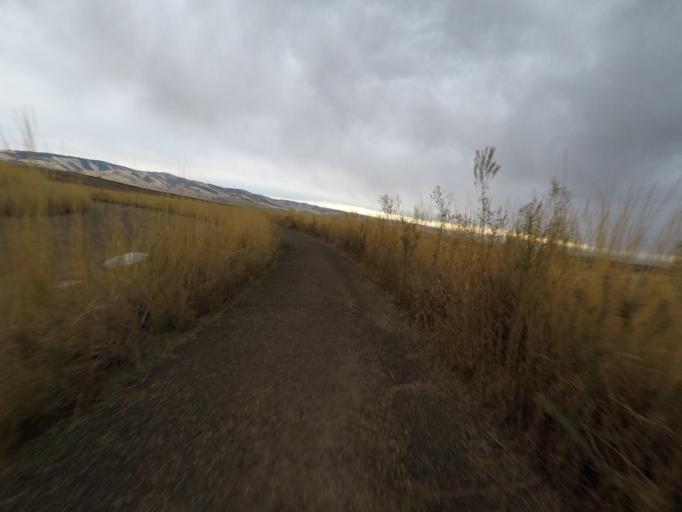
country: US
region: Washington
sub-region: Walla Walla County
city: Walla Walla East
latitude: 46.0630
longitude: -118.2681
